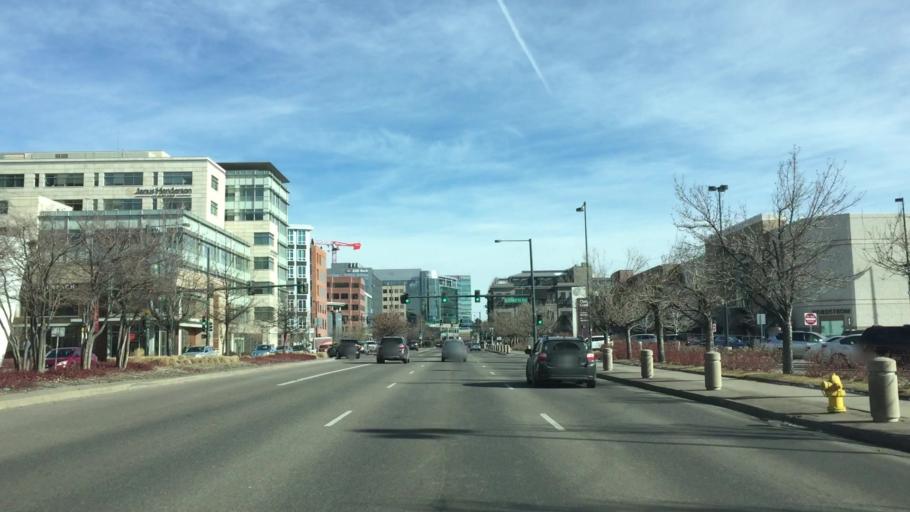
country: US
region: Colorado
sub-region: Arapahoe County
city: Glendale
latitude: 39.7180
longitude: -104.9569
